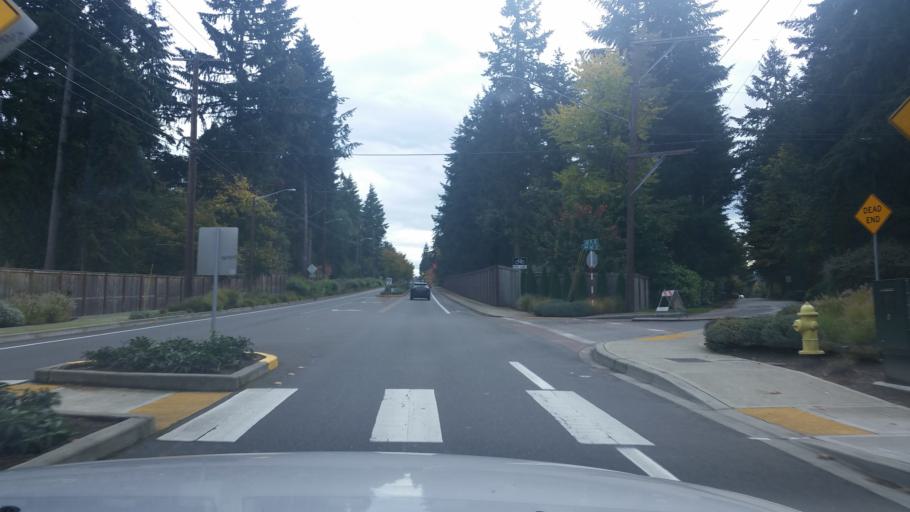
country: US
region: Washington
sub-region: King County
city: Eastgate
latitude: 47.5931
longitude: -122.1481
